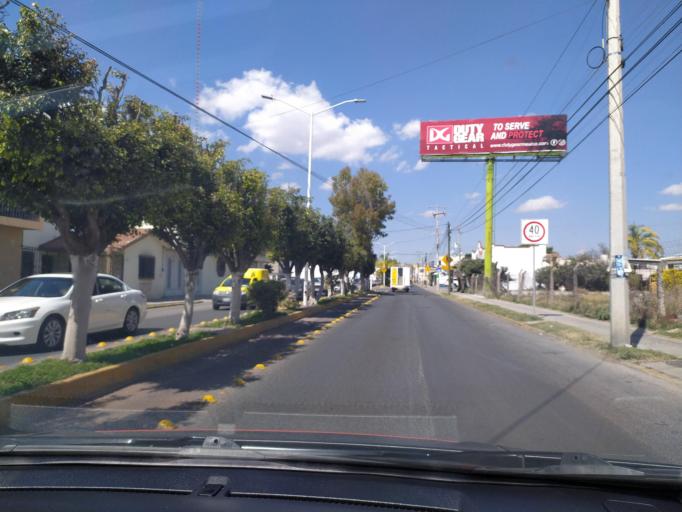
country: LA
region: Oudomxai
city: Muang La
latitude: 21.0258
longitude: 101.8520
